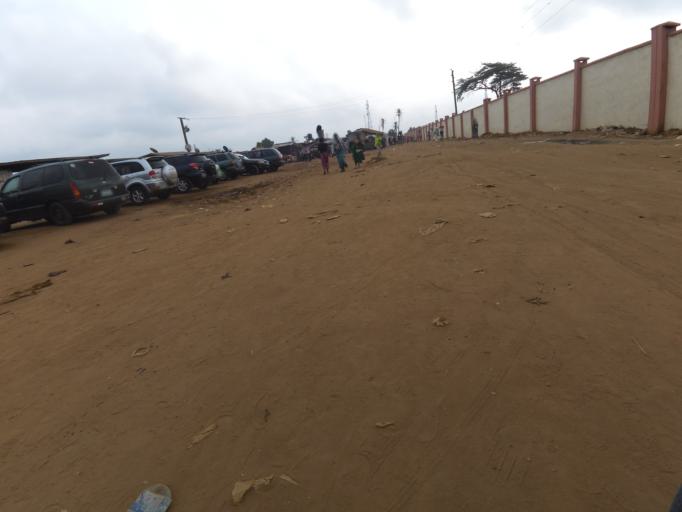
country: BJ
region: Queme
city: Porto-Novo
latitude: 6.3809
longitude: 2.7053
